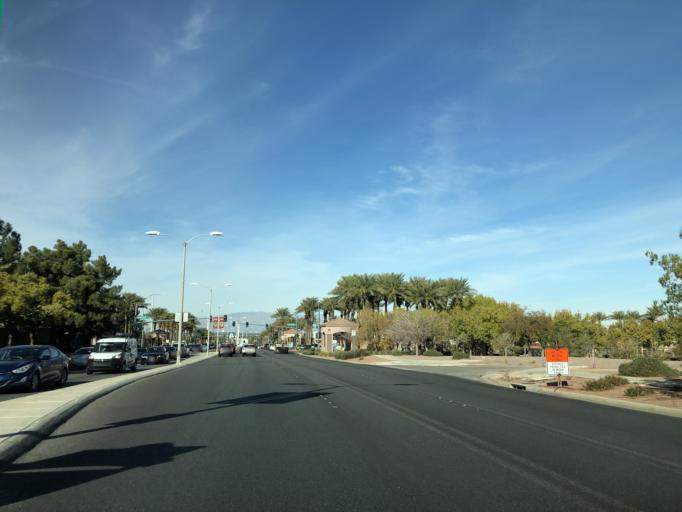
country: US
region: Nevada
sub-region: Clark County
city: Whitney
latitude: 36.0192
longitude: -115.0831
